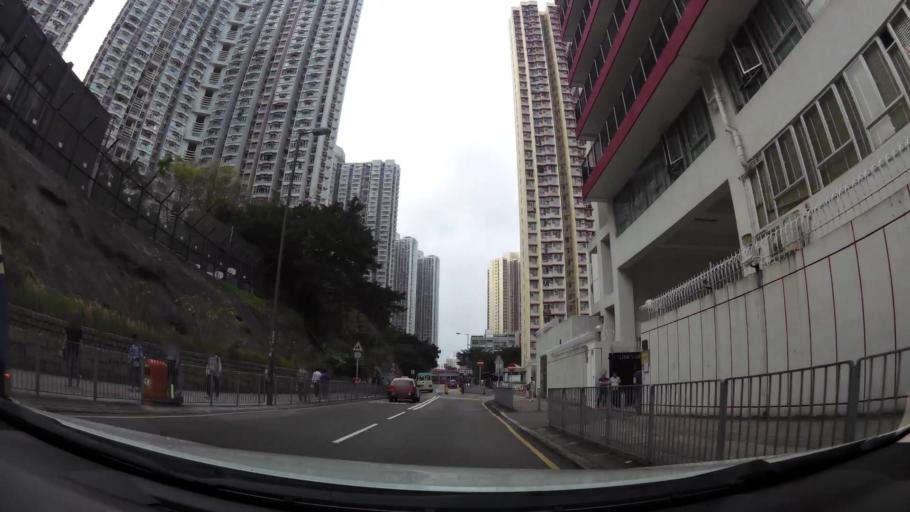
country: HK
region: Kowloon City
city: Kowloon
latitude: 22.3091
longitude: 114.2378
